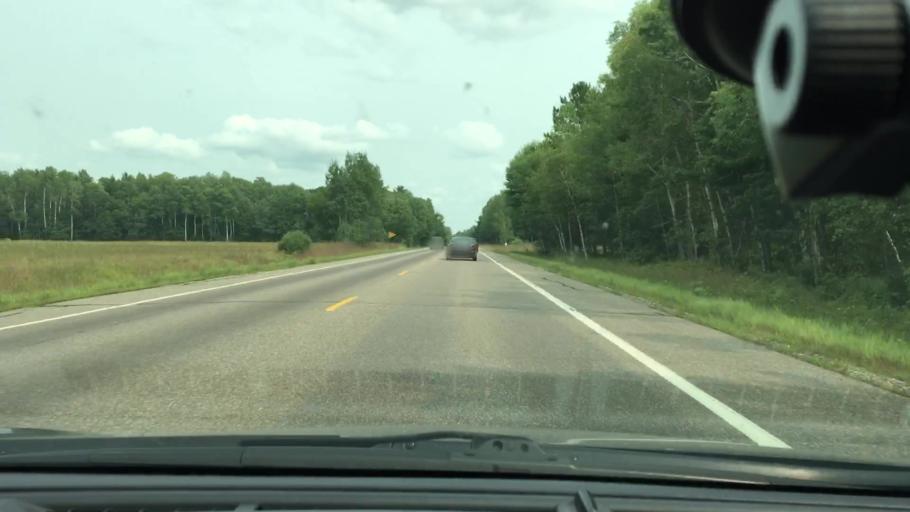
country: US
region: Minnesota
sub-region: Crow Wing County
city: Cross Lake
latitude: 46.7310
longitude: -94.0155
